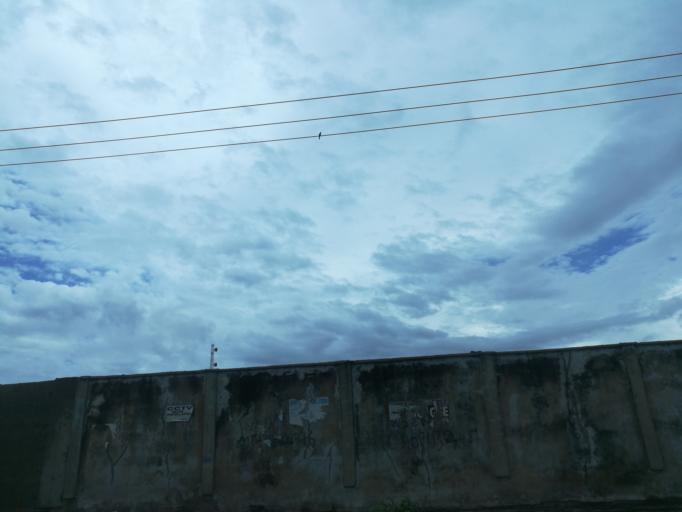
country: NG
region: Lagos
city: Ikoyi
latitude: 6.4389
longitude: 3.4746
